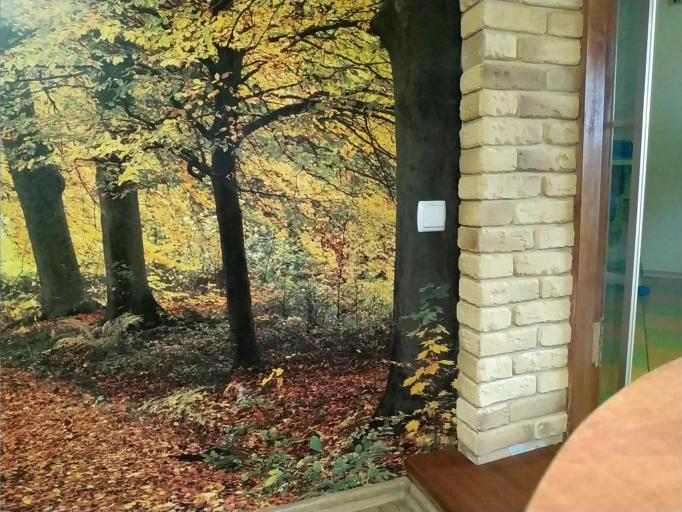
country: RU
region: Smolensk
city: Dorogobuzh
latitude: 54.9069
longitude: 33.3269
